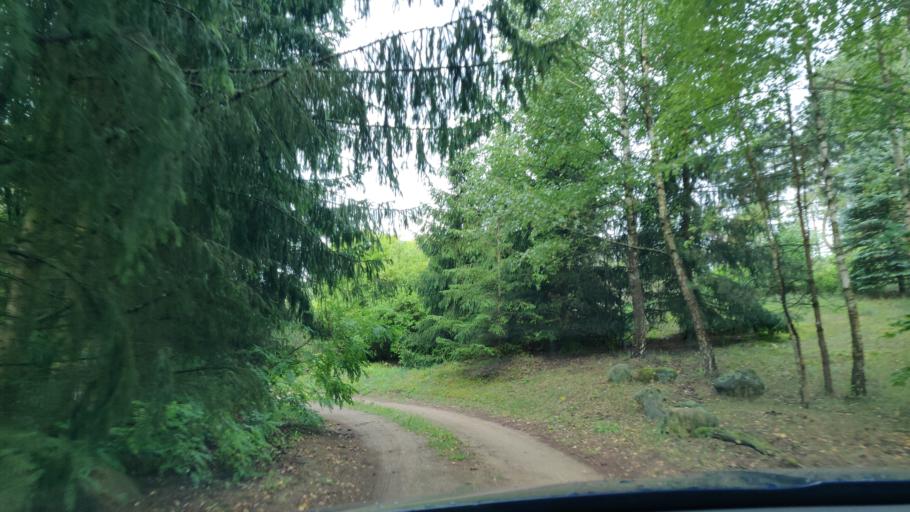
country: LT
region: Vilnius County
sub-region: Trakai
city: Rudiskes
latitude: 54.6105
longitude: 24.8220
